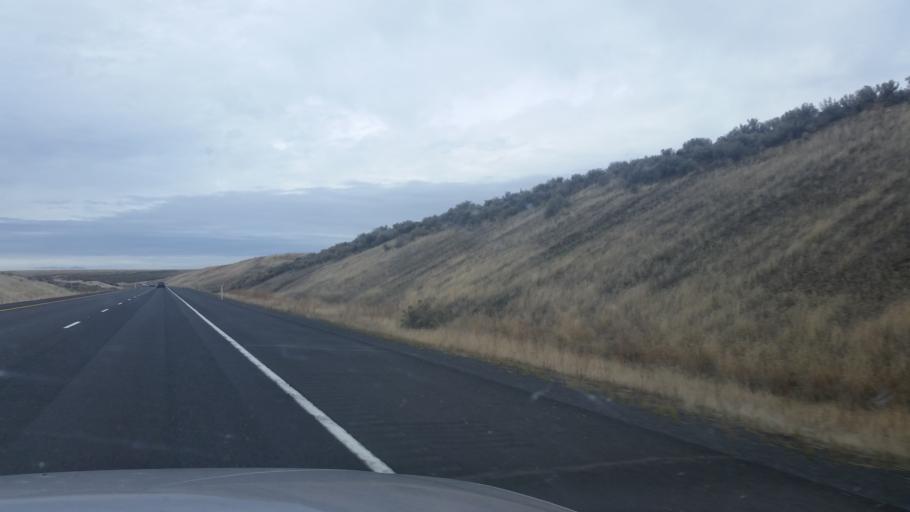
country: US
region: Washington
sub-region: Adams County
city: Ritzville
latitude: 47.1112
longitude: -118.5594
